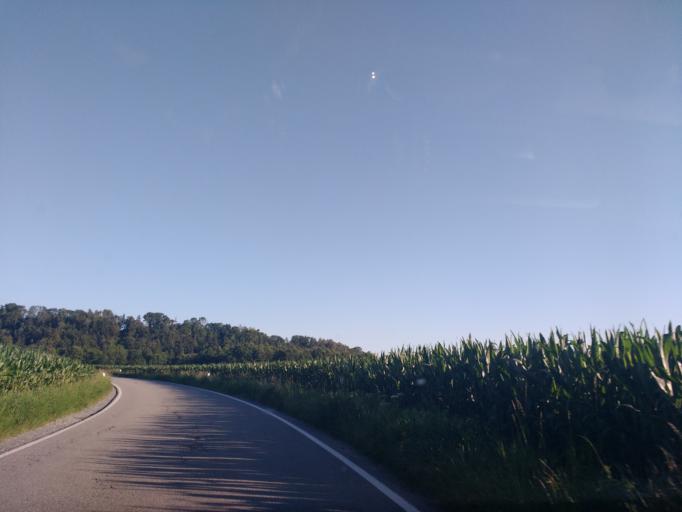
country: DE
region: Bavaria
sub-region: Upper Bavaria
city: Oberneukirchen
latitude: 48.2030
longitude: 12.4927
